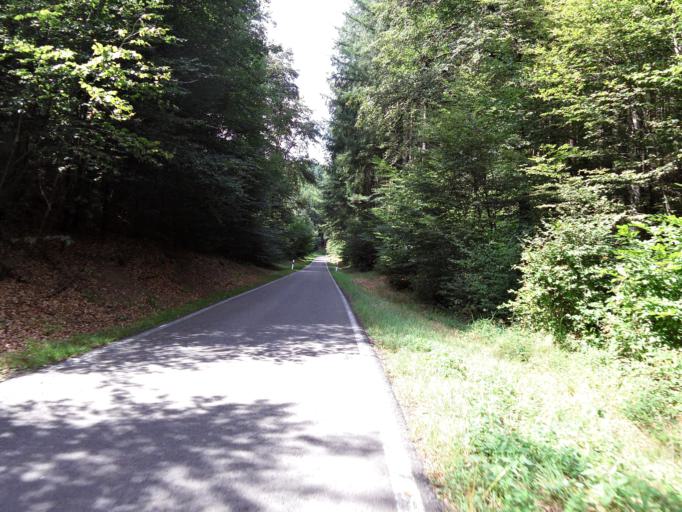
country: DE
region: Rheinland-Pfalz
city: Elmstein
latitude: 49.3862
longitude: 7.9317
